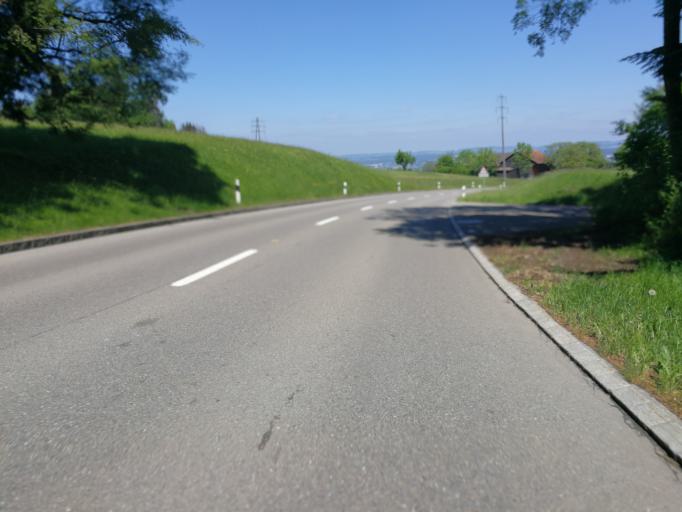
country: CH
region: Zurich
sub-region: Bezirk Uster
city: Esslingen
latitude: 47.2768
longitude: 8.6964
